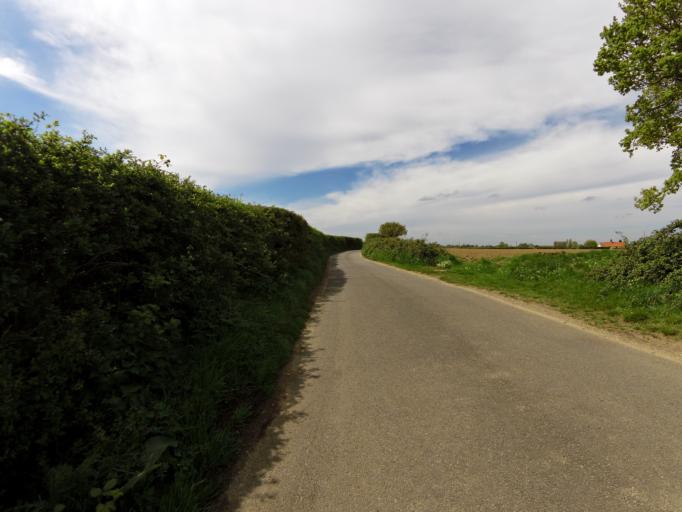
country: GB
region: England
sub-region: Suffolk
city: Ipswich
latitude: 52.0024
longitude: 1.1192
